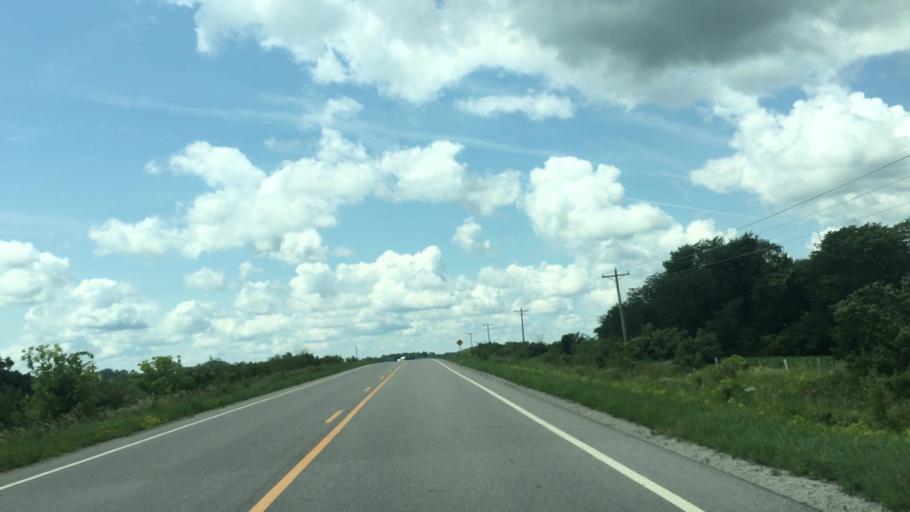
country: US
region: Iowa
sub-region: Johnson County
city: Solon
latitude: 41.8338
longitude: -91.4373
